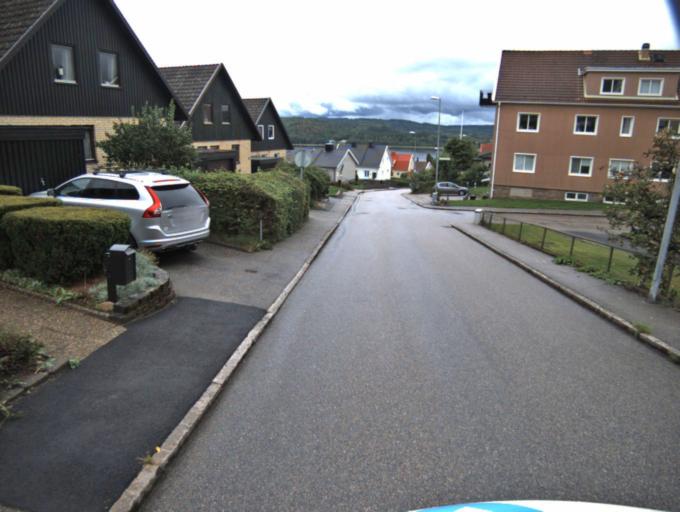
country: SE
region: Vaestra Goetaland
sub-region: Ulricehamns Kommun
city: Ulricehamn
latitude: 57.7917
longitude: 13.4206
